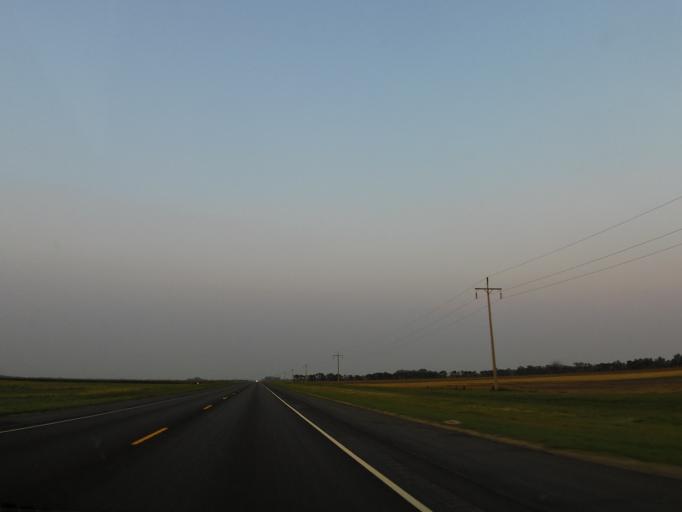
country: US
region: North Dakota
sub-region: Walsh County
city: Park River
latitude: 48.4127
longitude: -97.5783
